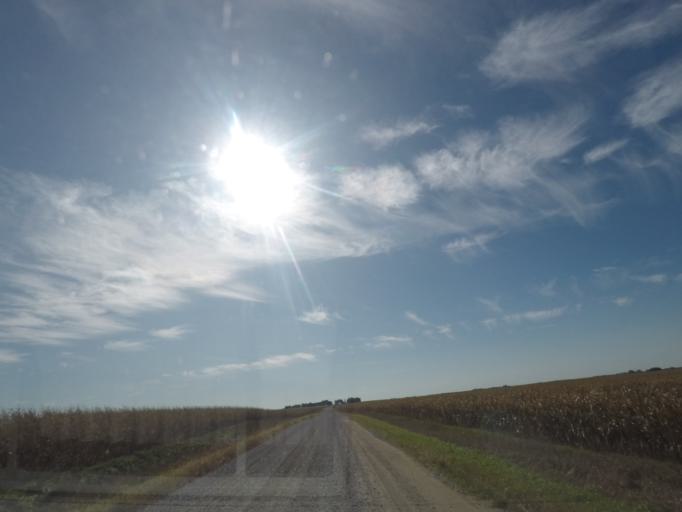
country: US
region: Iowa
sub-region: Story County
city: Nevada
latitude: 42.0624
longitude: -93.3295
